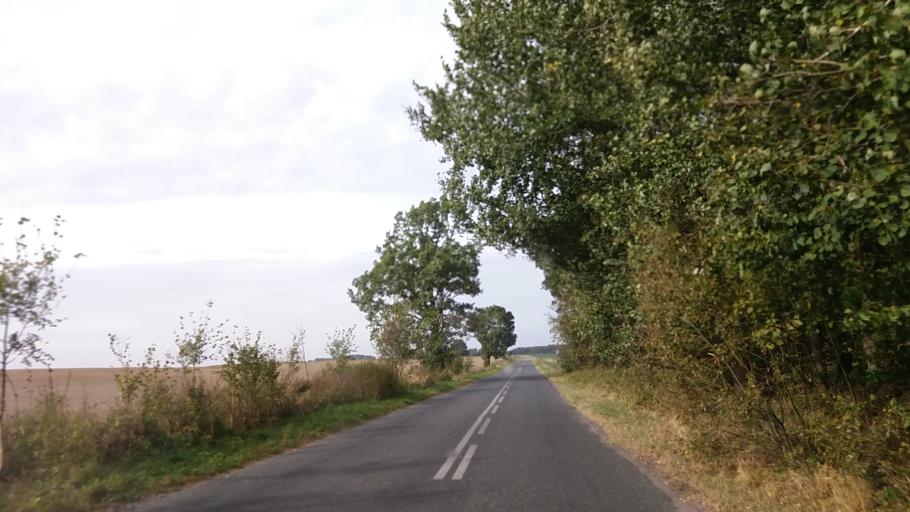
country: PL
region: West Pomeranian Voivodeship
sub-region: Powiat choszczenski
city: Krzecin
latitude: 53.0327
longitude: 15.5018
